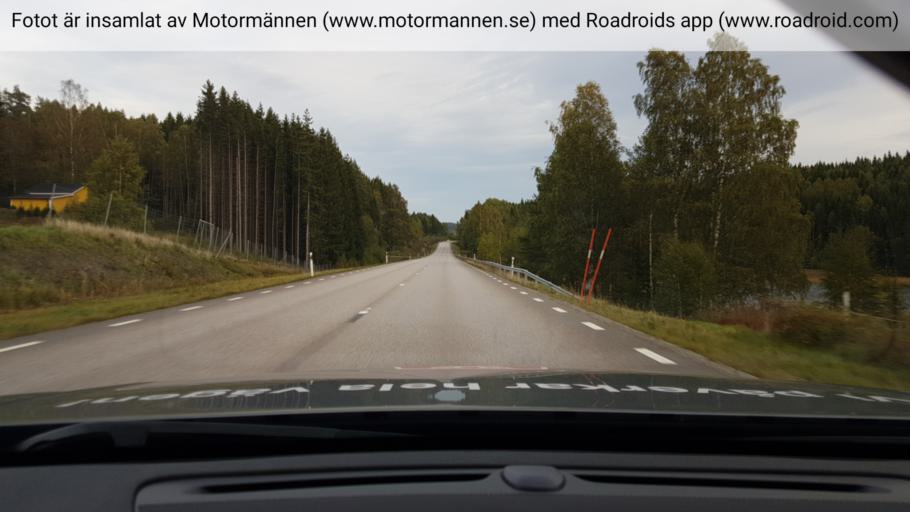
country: SE
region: Vaestra Goetaland
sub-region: Bengtsfors Kommun
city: Billingsfors
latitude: 59.0287
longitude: 12.3432
